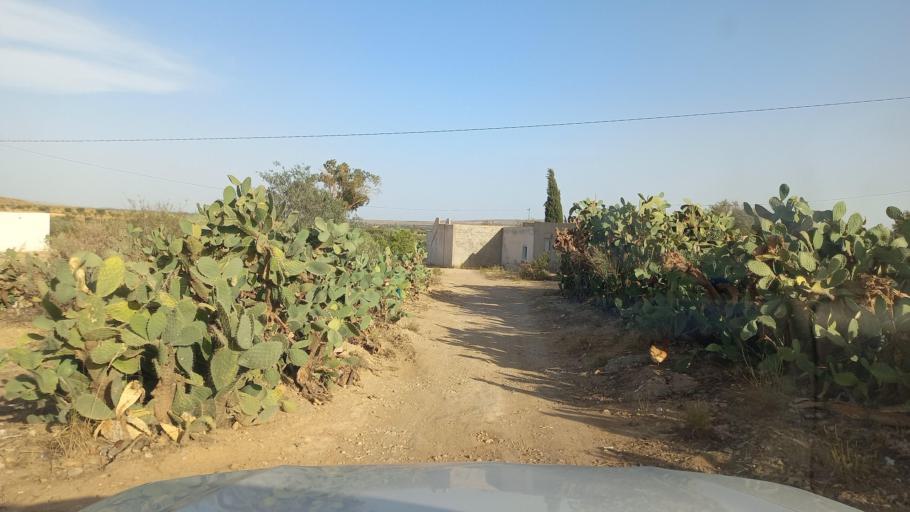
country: TN
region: Al Qasrayn
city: Kasserine
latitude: 35.2377
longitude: 8.9179
